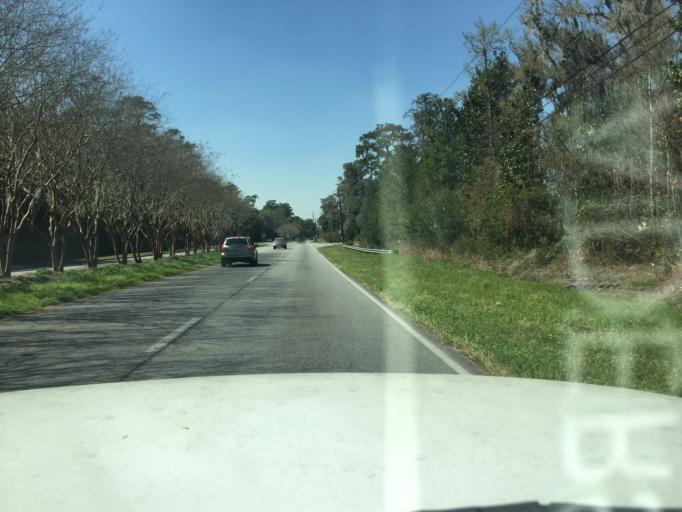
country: US
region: Georgia
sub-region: Chatham County
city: Whitemarsh Island
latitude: 32.0364
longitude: -81.0116
